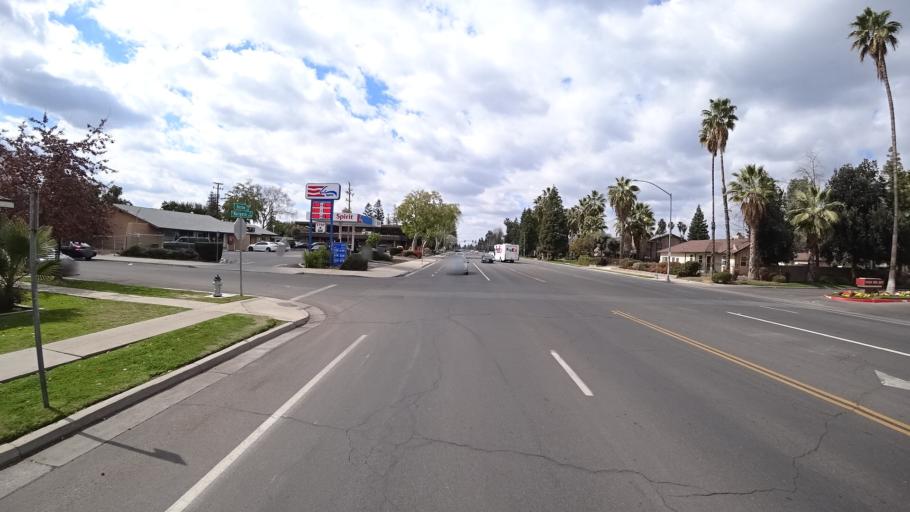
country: US
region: California
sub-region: Fresno County
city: Fresno
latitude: 36.8157
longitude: -119.7790
